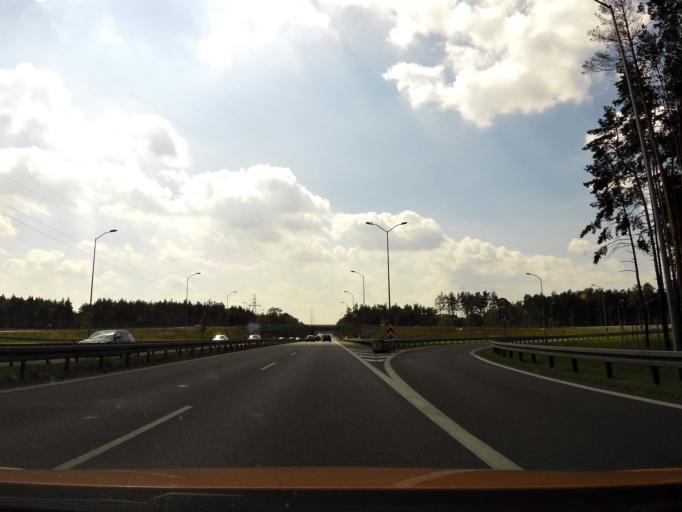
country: PL
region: West Pomeranian Voivodeship
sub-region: Powiat gryfinski
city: Stare Czarnowo
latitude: 53.3970
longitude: 14.7193
